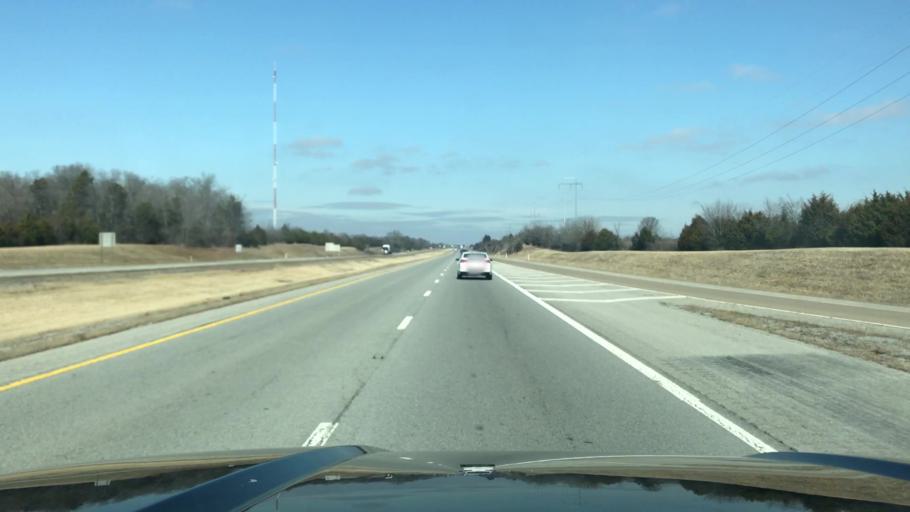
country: US
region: Tennessee
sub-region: Wilson County
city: Rural Hill
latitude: 36.0720
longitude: -86.4297
